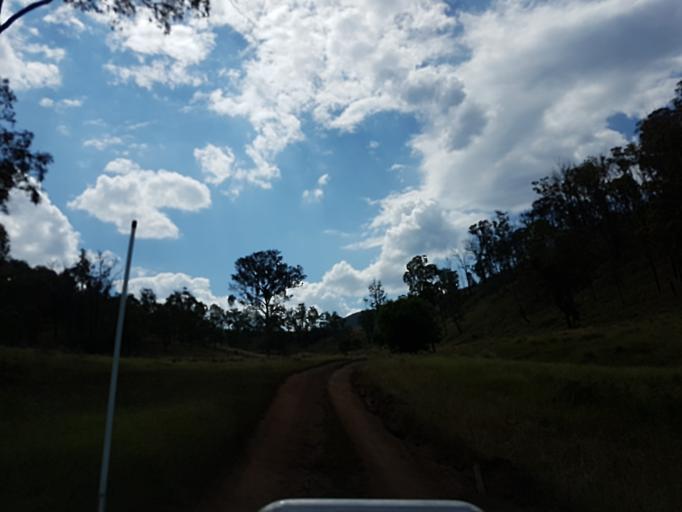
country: AU
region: Victoria
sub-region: East Gippsland
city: Lakes Entrance
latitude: -37.4005
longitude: 148.3289
